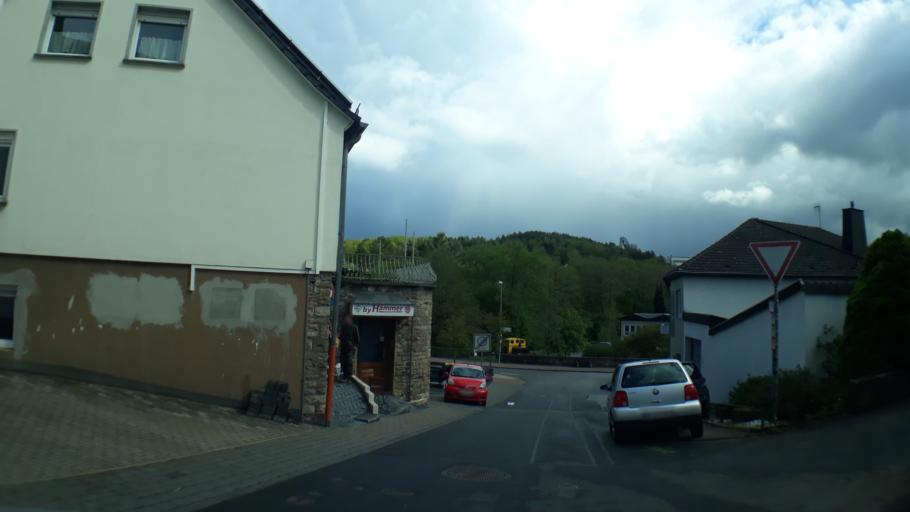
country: DE
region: North Rhine-Westphalia
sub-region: Regierungsbezirk Koln
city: Kall
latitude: 50.5253
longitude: 6.5558
